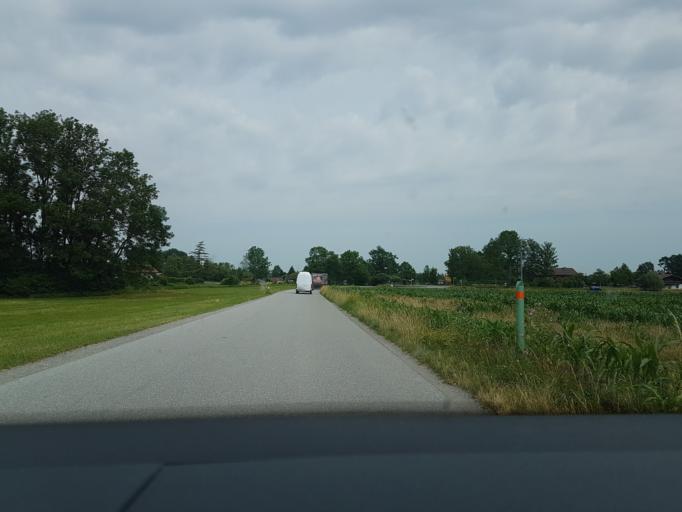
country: DE
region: Bavaria
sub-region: Upper Bavaria
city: Flintsbach
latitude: 47.7357
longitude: 12.1249
